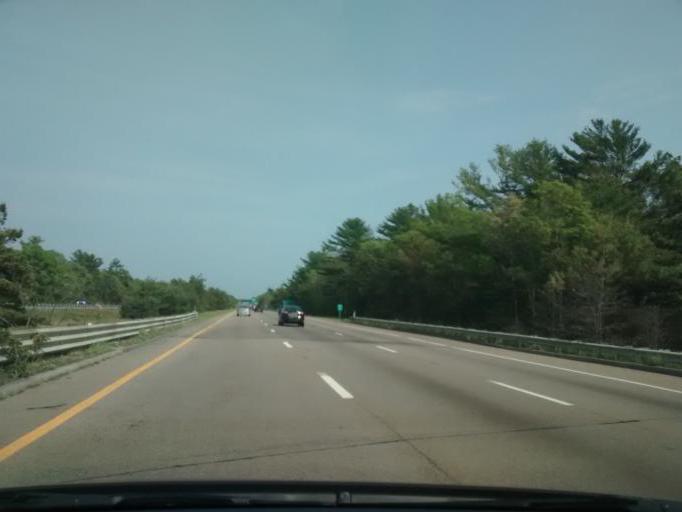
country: US
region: Massachusetts
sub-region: Plymouth County
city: Wareham Center
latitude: 41.7796
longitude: -70.7190
